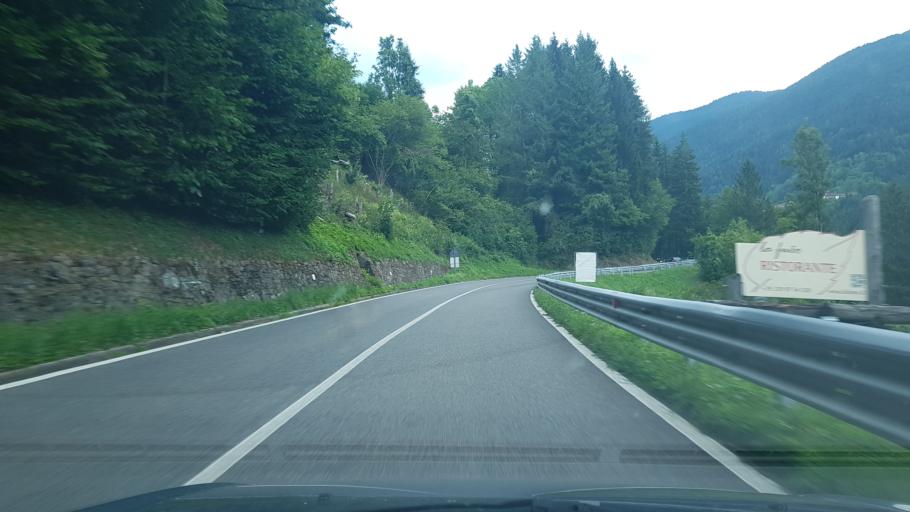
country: IT
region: Friuli Venezia Giulia
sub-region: Provincia di Udine
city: Rigolato
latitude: 46.5429
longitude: 12.8616
